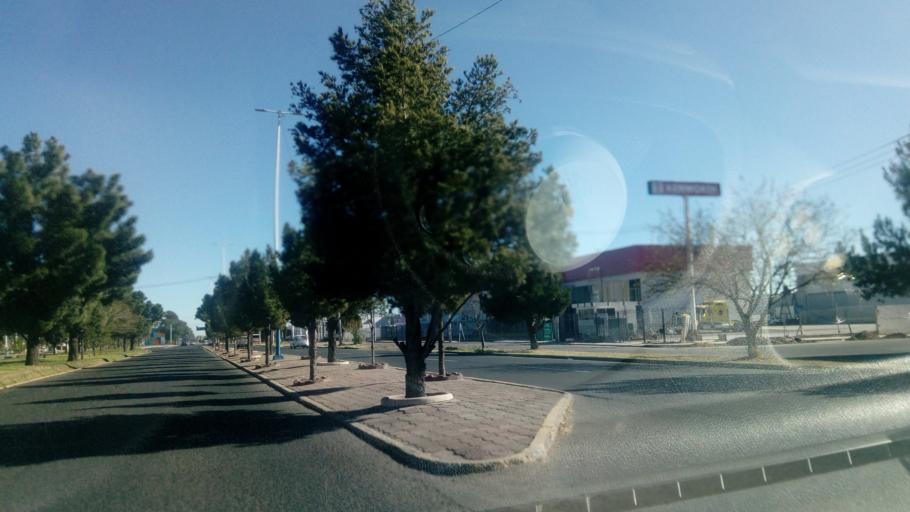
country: MX
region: Durango
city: Victoria de Durango
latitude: 24.0623
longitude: -104.6065
